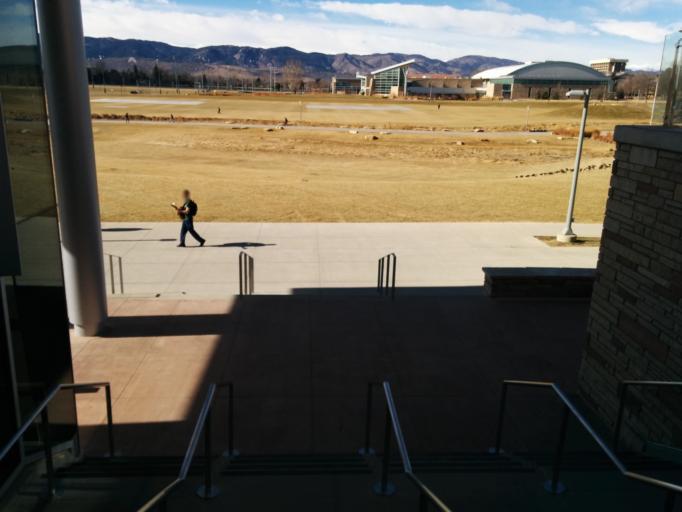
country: US
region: Colorado
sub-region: Larimer County
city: Fort Collins
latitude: 40.5746
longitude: -105.0852
